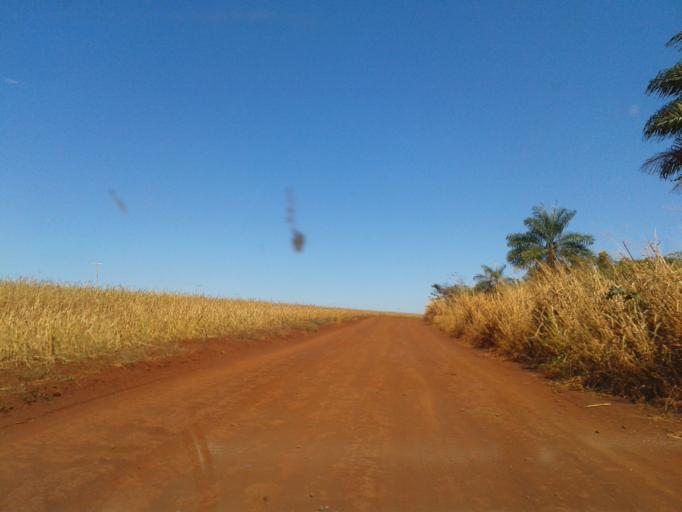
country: BR
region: Minas Gerais
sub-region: Centralina
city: Centralina
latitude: -18.5890
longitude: -49.1505
